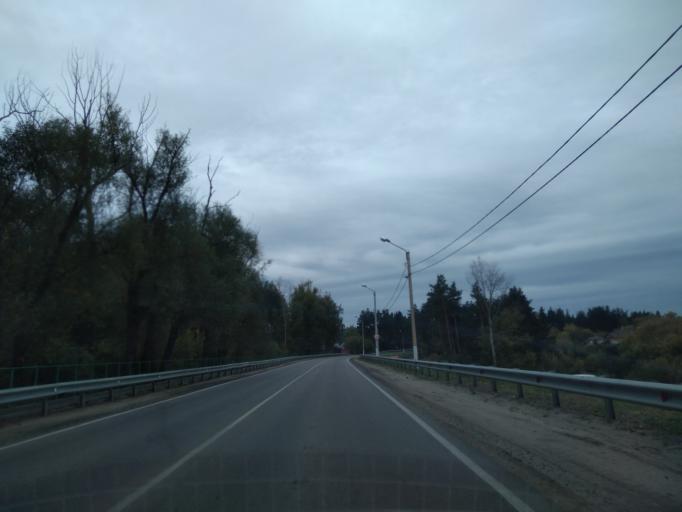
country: RU
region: Lipetsk
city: Zadonsk
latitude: 52.3877
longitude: 38.9351
